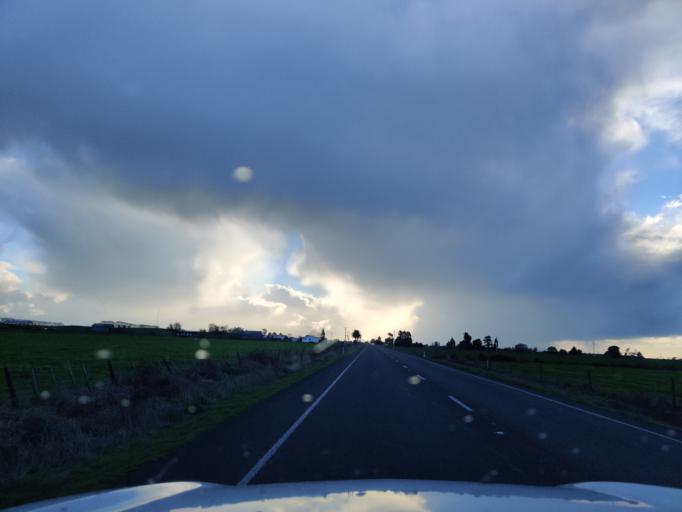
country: NZ
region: Waikato
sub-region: Hamilton City
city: Hamilton
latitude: -37.6930
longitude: 175.4313
